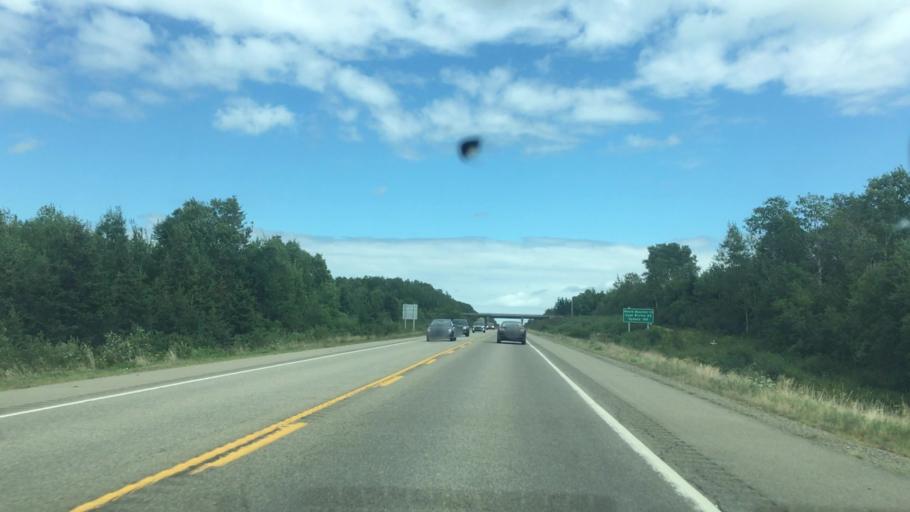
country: CA
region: Nova Scotia
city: Port Hawkesbury
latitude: 45.6175
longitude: -61.6178
